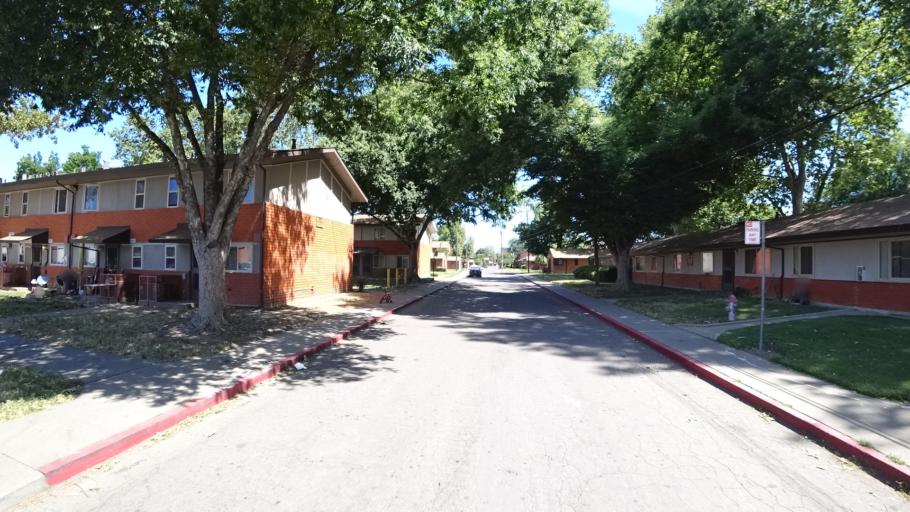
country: US
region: California
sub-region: Sacramento County
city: Sacramento
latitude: 38.5617
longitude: -121.5061
